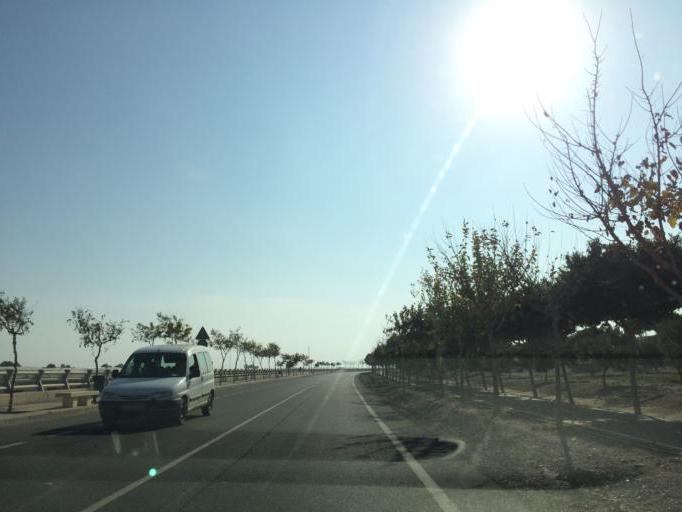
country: ES
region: Andalusia
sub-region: Provincia de Almeria
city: Almeria
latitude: 36.8309
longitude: -2.4280
